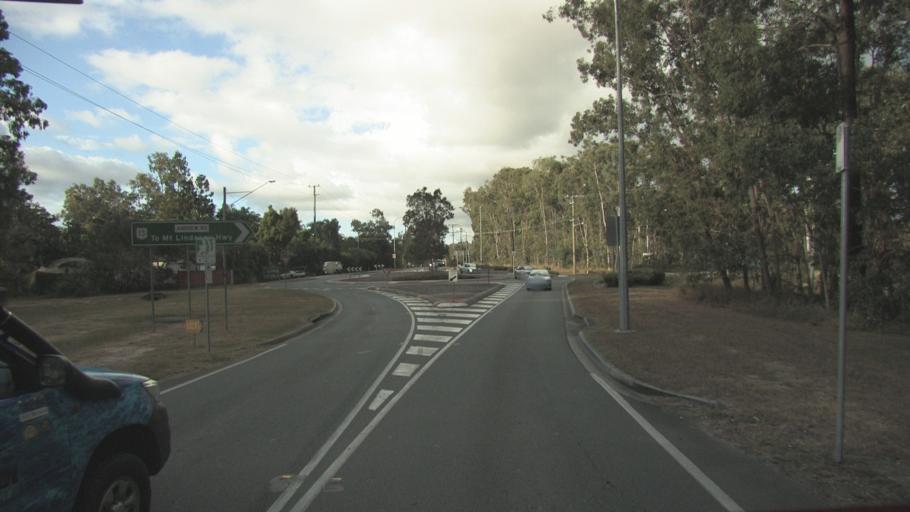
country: AU
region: Queensland
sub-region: Logan
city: Park Ridge South
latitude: -27.7071
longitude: 153.0026
